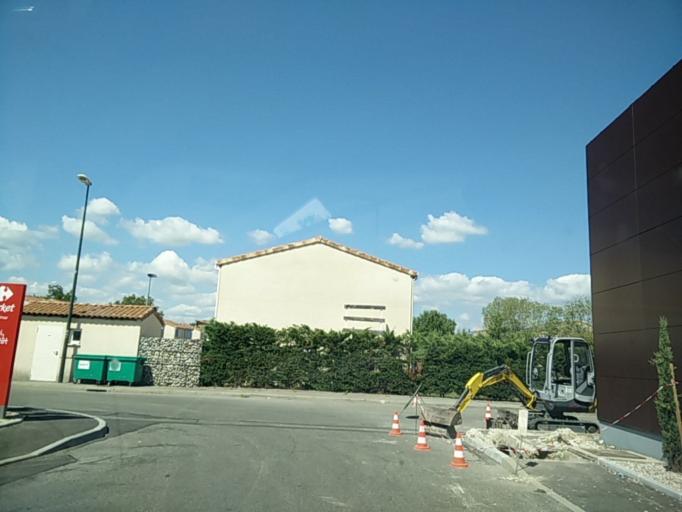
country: FR
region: Rhone-Alpes
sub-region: Departement de la Drome
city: Montelimar
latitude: 44.5518
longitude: 4.7691
